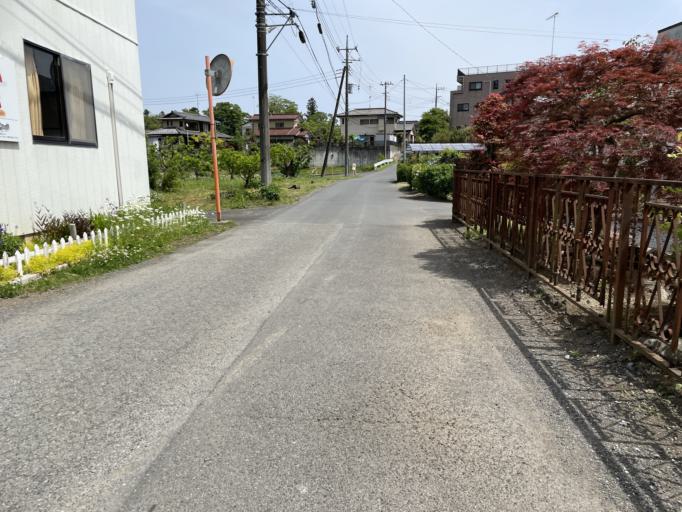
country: JP
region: Saitama
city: Hanno
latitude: 35.8908
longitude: 139.3185
